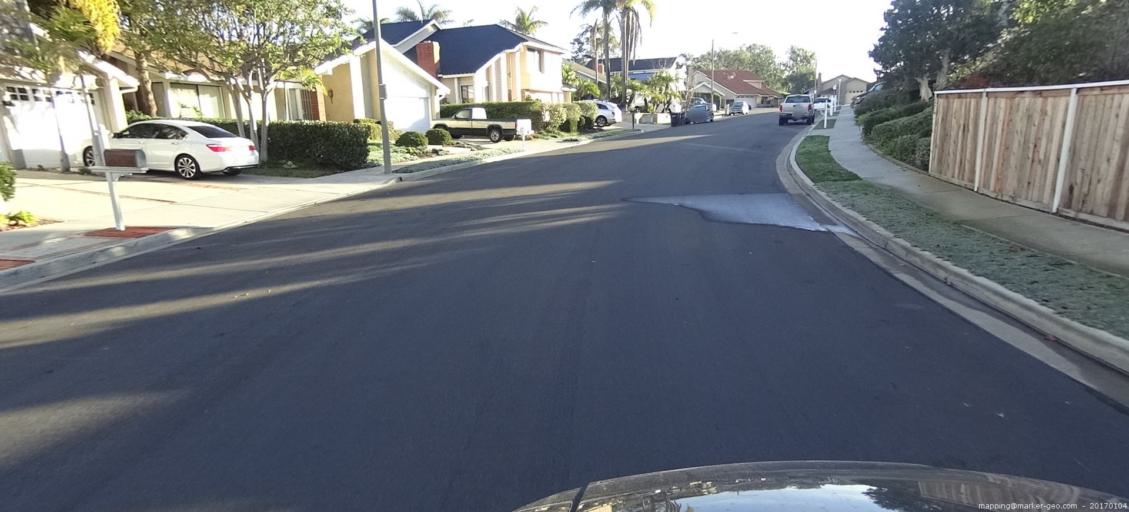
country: US
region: California
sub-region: Orange County
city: Dana Point
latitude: 33.4835
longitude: -117.7000
